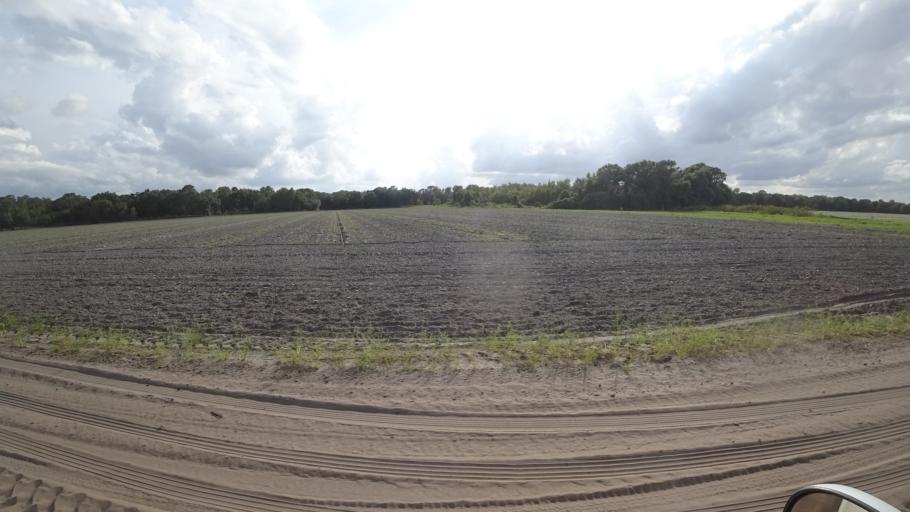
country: US
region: Florida
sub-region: Hillsborough County
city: Wimauma
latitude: 27.6034
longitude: -82.1405
